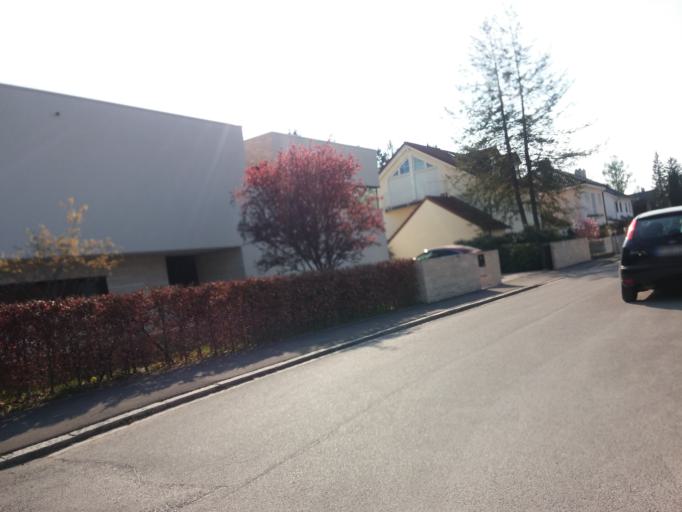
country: DE
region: Bavaria
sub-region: Upper Bavaria
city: Neubiberg
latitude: 48.0977
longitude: 11.6805
